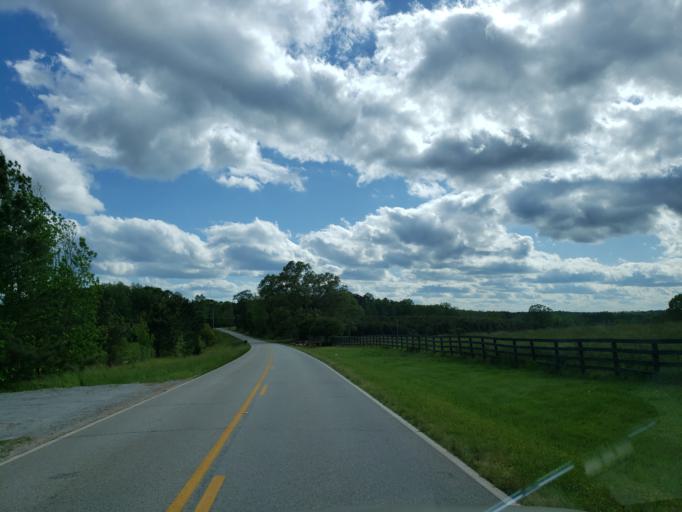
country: US
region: Georgia
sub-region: Carroll County
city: Mount Zion
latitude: 33.6704
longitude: -85.1946
